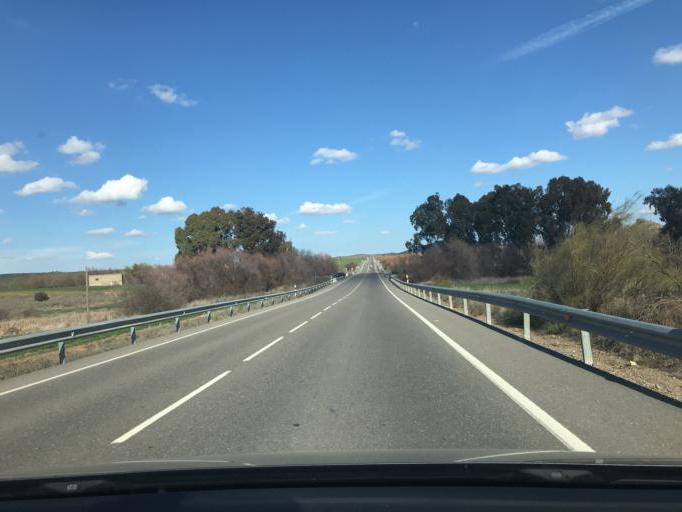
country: ES
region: Andalusia
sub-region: Province of Cordoba
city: Fuente Obejuna
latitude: 38.2924
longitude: -5.3509
